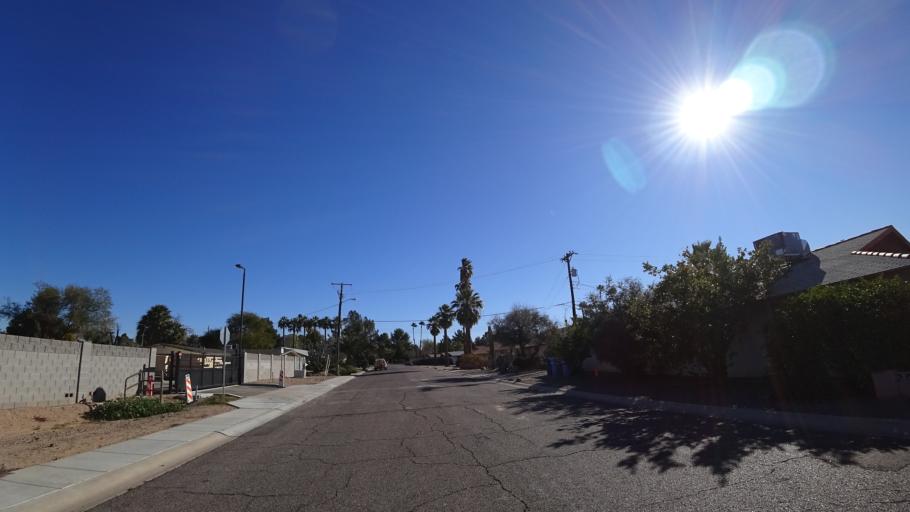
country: US
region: Arizona
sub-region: Maricopa County
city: Phoenix
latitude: 33.4996
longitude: -112.0237
